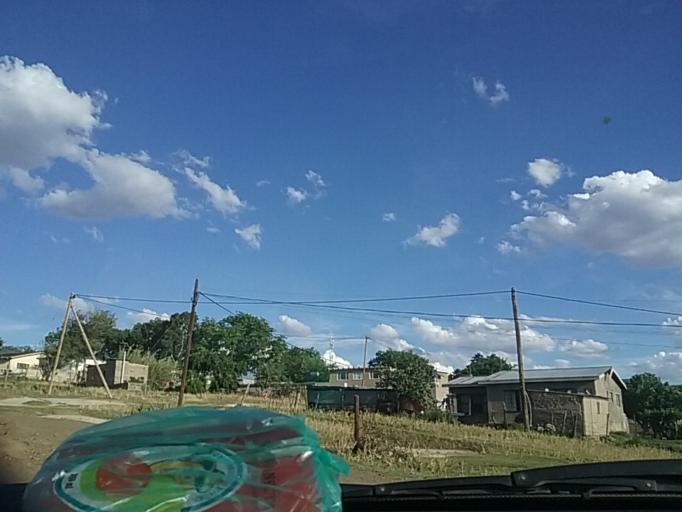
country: LS
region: Berea
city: Teyateyaneng
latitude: -29.1494
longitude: 27.7394
